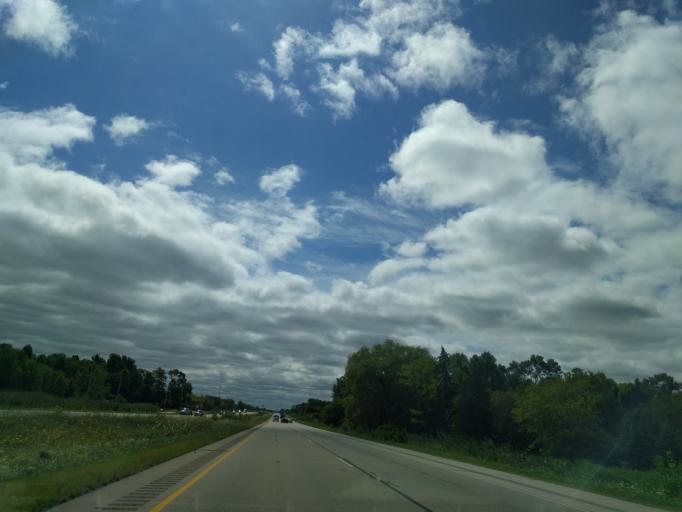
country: US
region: Wisconsin
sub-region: Brown County
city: Suamico
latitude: 44.7021
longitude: -88.0509
